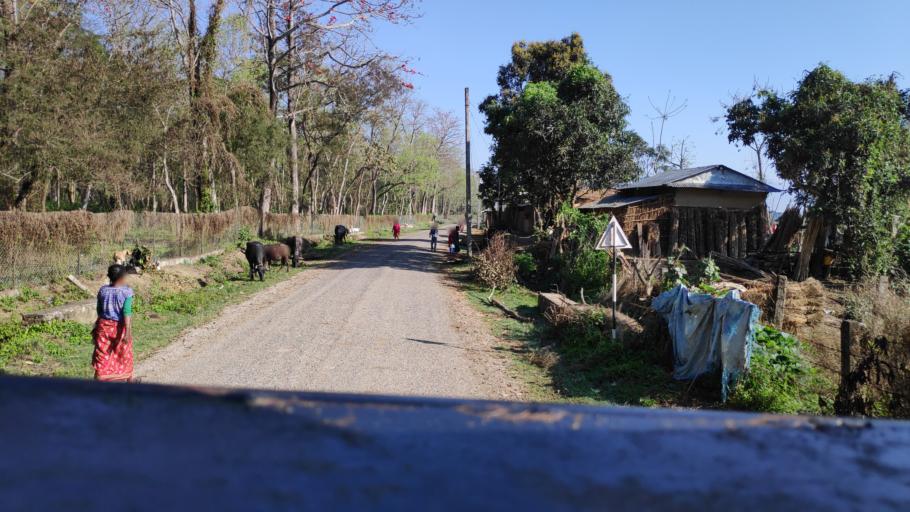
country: NP
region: Central Region
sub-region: Narayani Zone
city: Bharatpur
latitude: 27.5706
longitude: 84.5174
